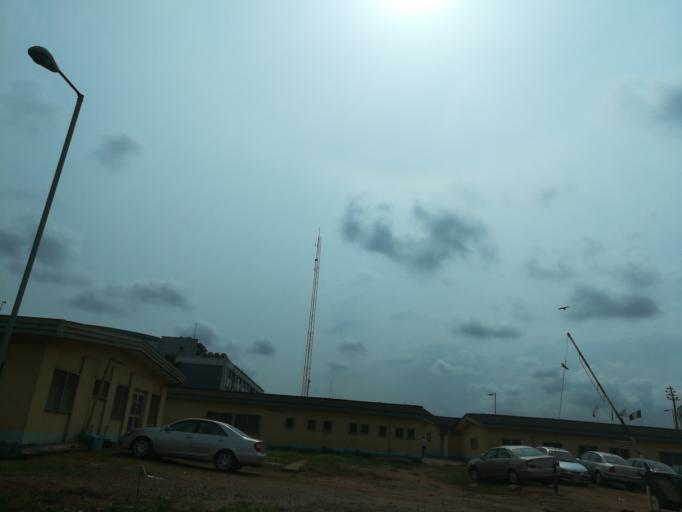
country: NG
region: Lagos
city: Oshodi
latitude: 6.5753
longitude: 3.3245
